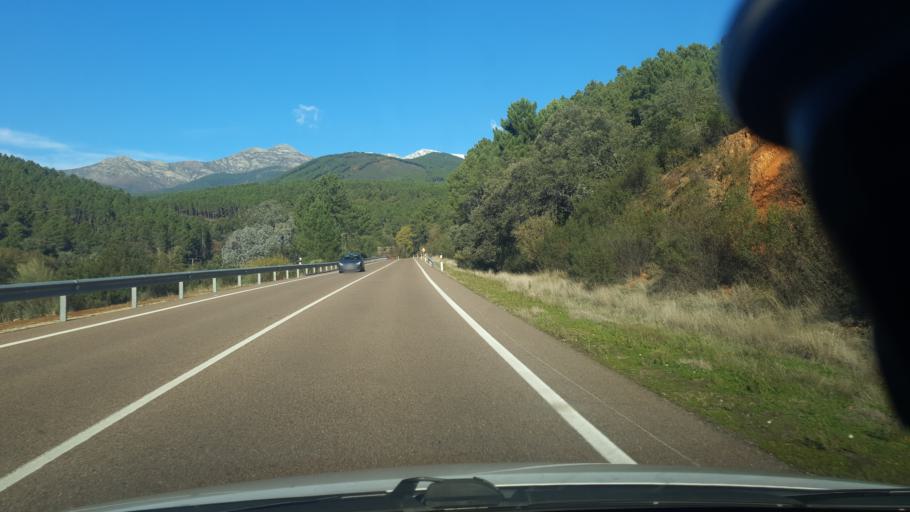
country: ES
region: Castille and Leon
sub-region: Provincia de Avila
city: Poyales del Hoyo
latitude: 40.1648
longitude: -5.1201
